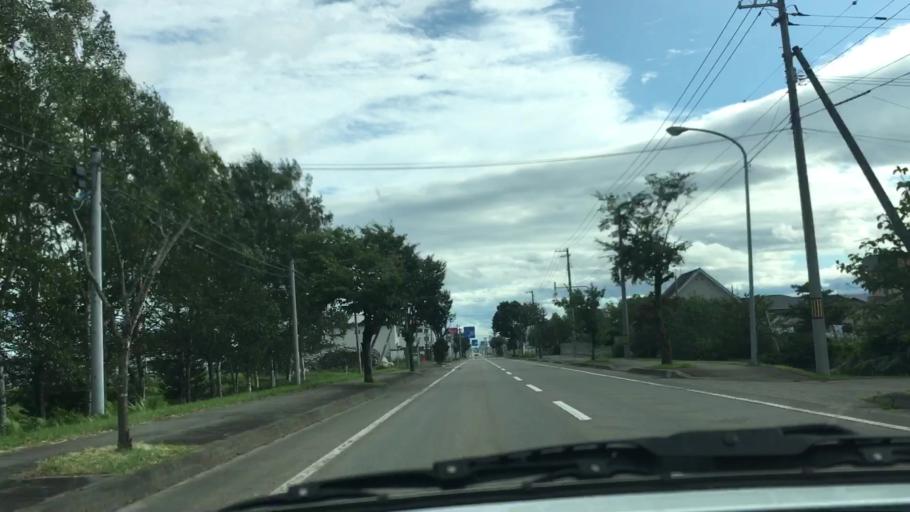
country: JP
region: Hokkaido
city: Otofuke
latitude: 43.2388
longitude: 143.2964
